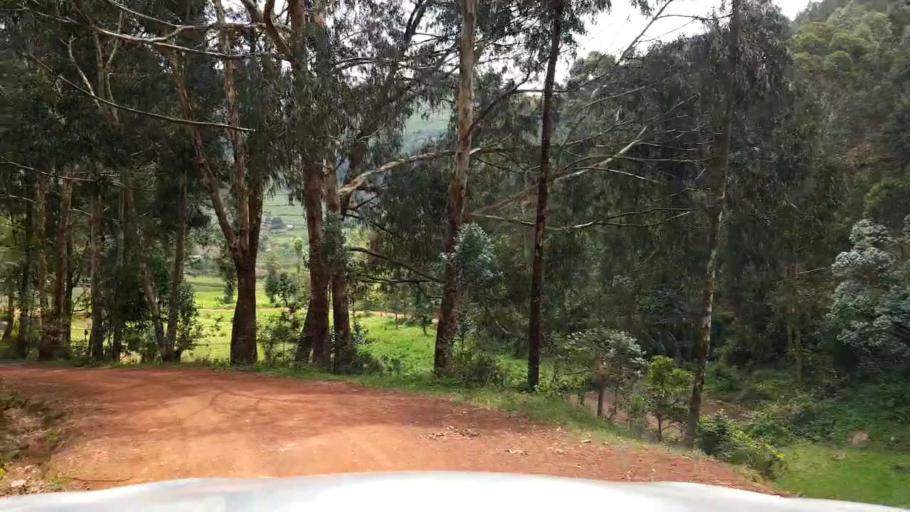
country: RW
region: Northern Province
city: Byumba
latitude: -1.4802
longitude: 29.9069
